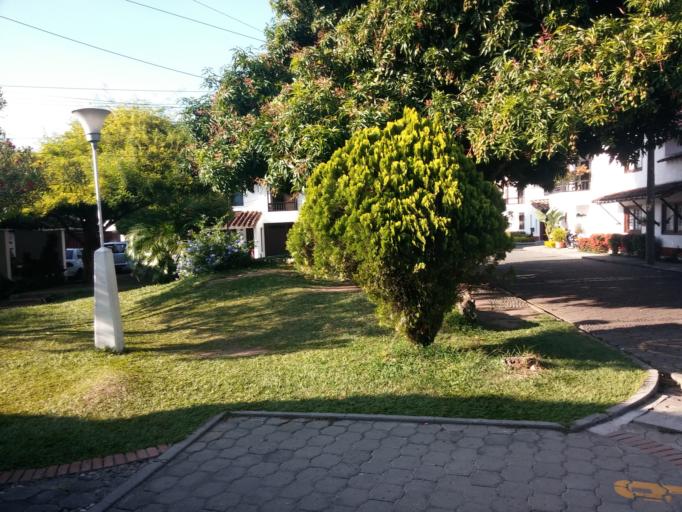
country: CO
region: Valle del Cauca
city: Cartago
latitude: 4.7554
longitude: -75.9188
